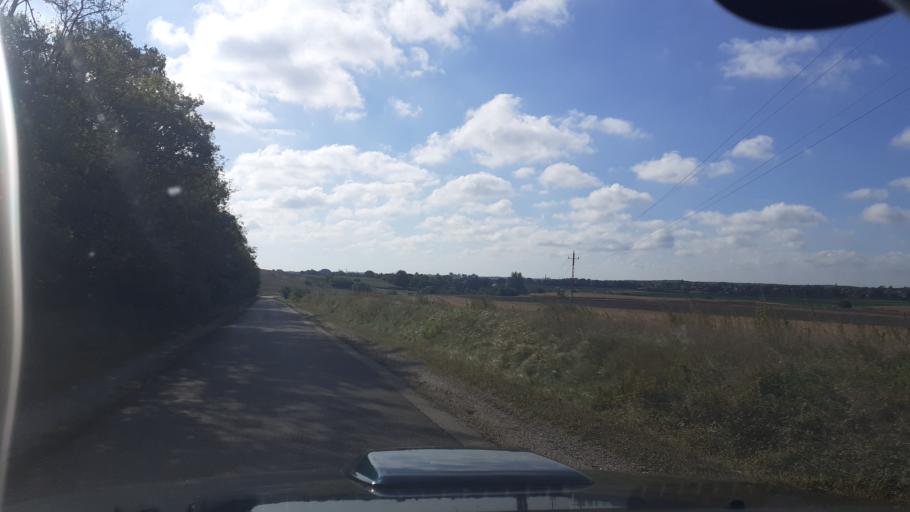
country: HU
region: Fejer
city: Baracs
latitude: 46.9290
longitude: 18.8739
